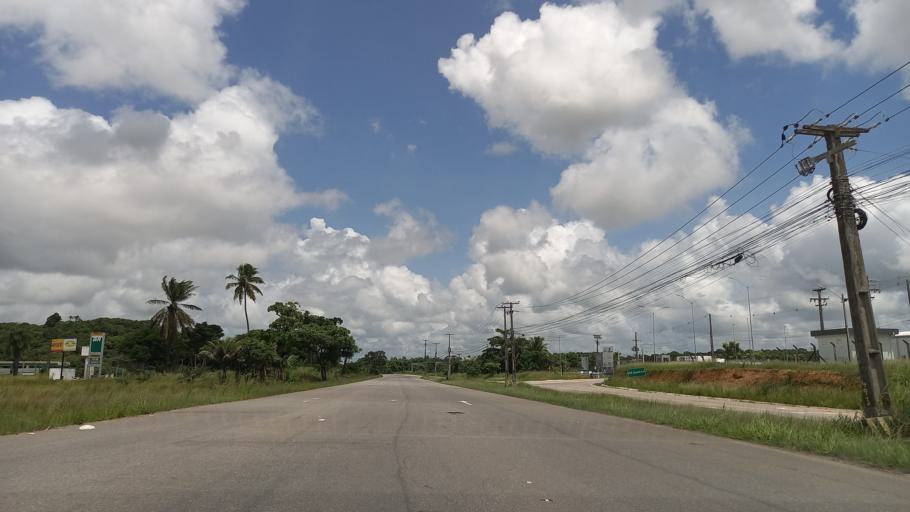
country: BR
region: Pernambuco
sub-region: Ipojuca
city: Ipojuca
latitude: -8.3583
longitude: -35.0202
